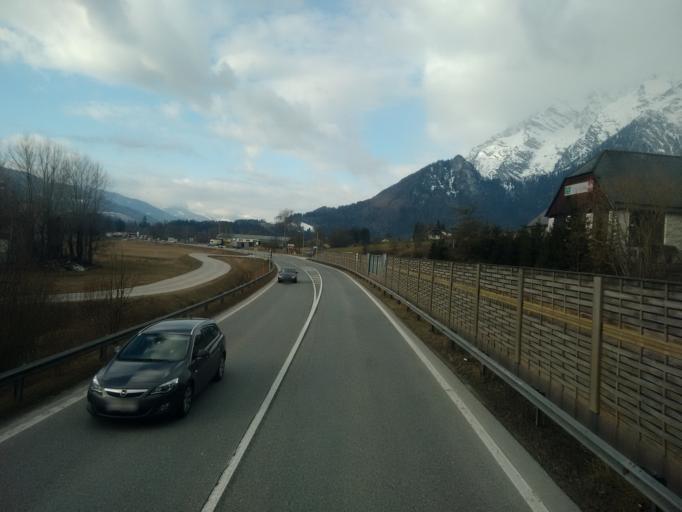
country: AT
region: Styria
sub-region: Politischer Bezirk Liezen
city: Stainach
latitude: 47.5277
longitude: 14.0887
